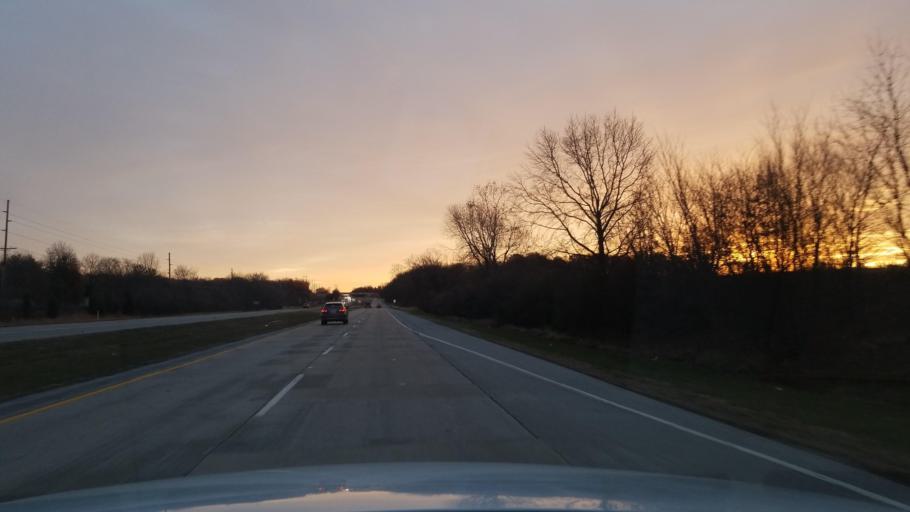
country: US
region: Indiana
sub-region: Posey County
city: Mount Vernon
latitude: 37.9418
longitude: -87.7502
